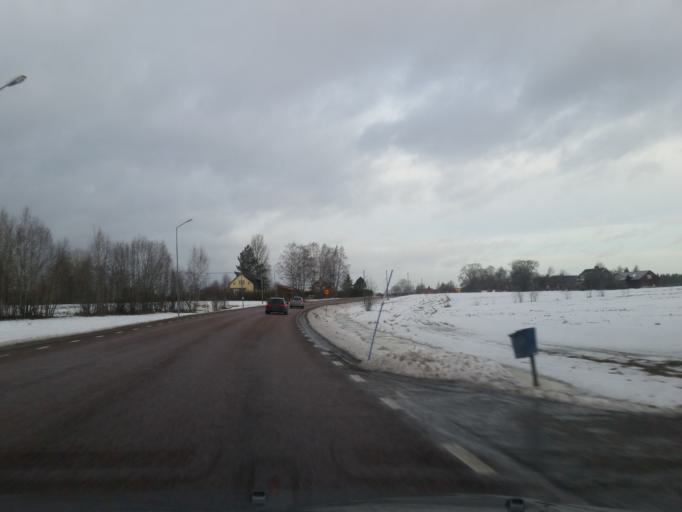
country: SE
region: Gaevleborg
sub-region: Sandvikens Kommun
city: Jarbo
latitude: 60.6714
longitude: 16.6728
